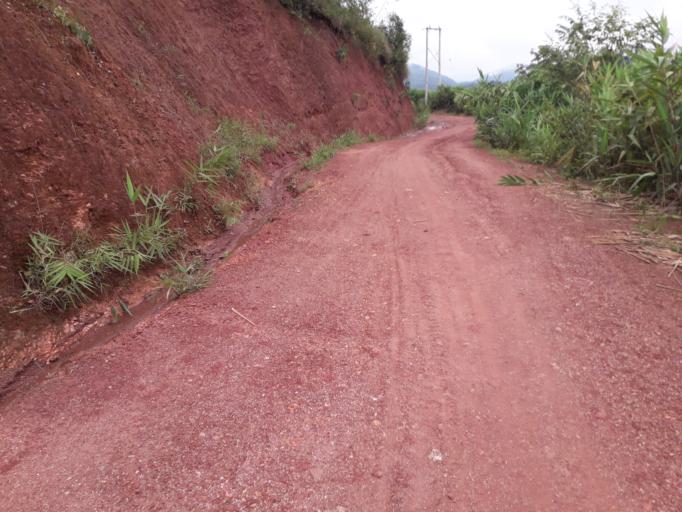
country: CN
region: Yunnan
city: Menglie
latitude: 22.2638
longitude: 101.5811
